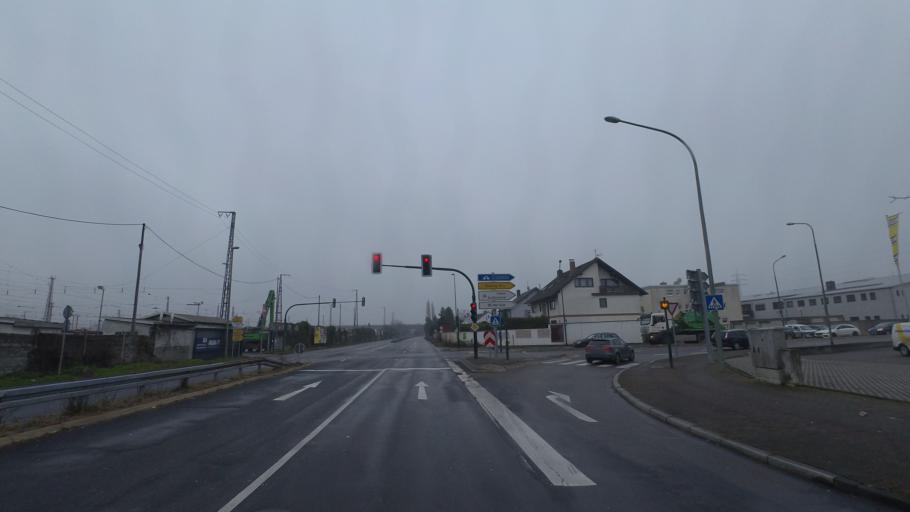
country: DE
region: Hesse
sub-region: Regierungsbezirk Darmstadt
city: Hanau am Main
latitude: 50.1183
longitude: 8.9311
